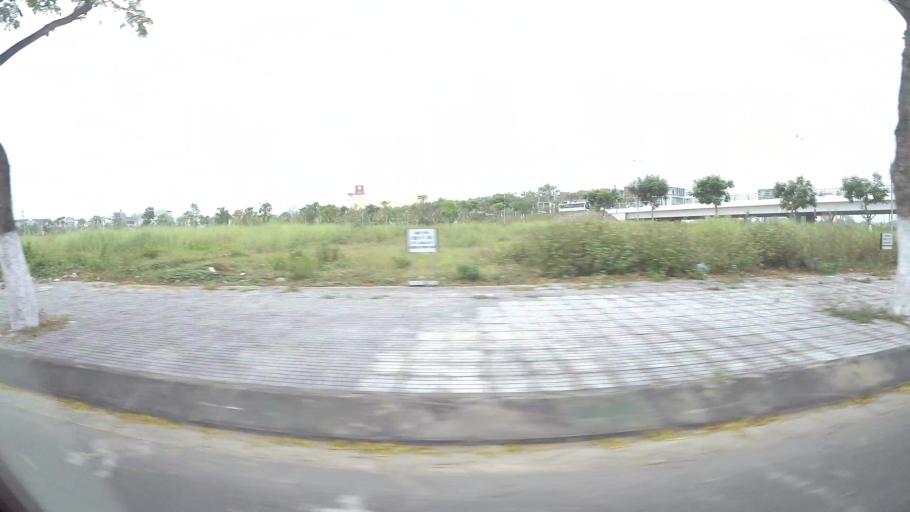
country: VN
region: Da Nang
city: Ngu Hanh Son
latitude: 16.0341
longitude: 108.2340
